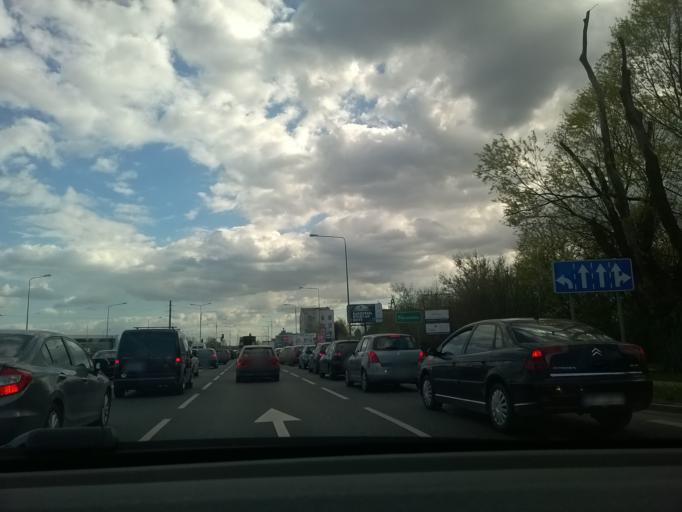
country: PL
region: Masovian Voivodeship
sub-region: Powiat piaseczynski
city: Mysiadlo
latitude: 52.0994
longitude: 21.0187
